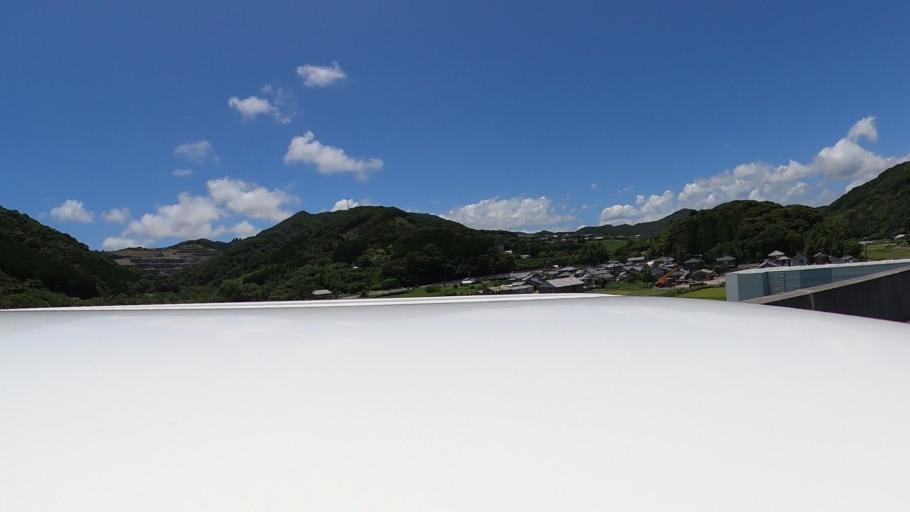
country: JP
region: Miyazaki
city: Nobeoka
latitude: 32.3981
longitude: 131.6184
